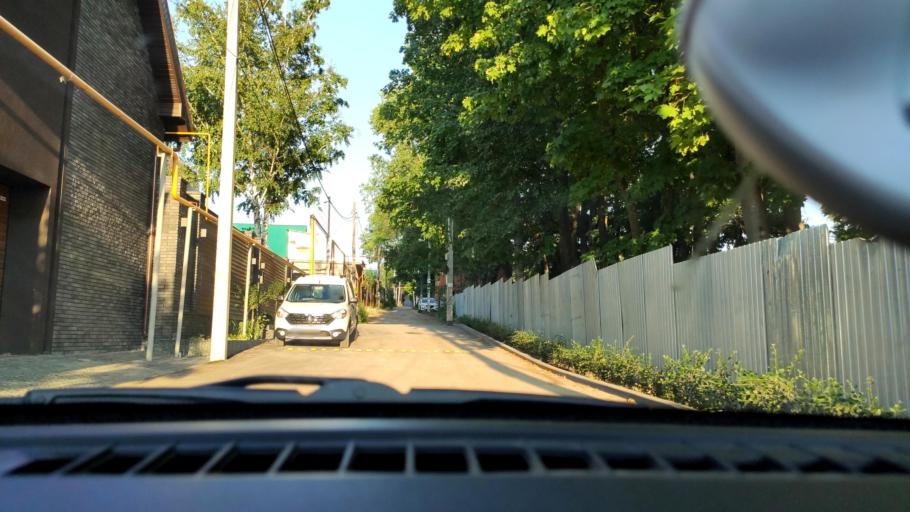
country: RU
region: Samara
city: Samara
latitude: 53.2750
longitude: 50.2087
